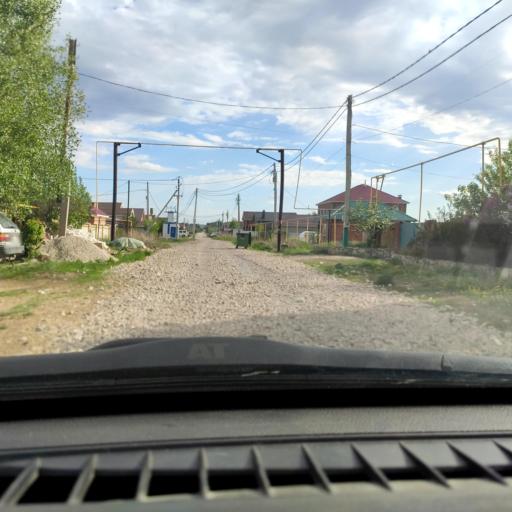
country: RU
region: Samara
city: Tol'yatti
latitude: 53.5666
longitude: 49.4079
